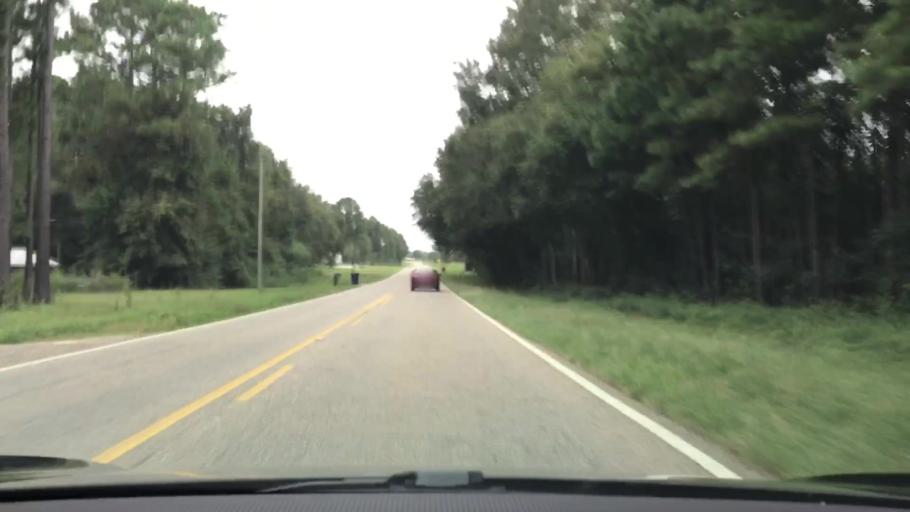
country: US
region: Alabama
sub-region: Geneva County
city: Samson
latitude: 31.1697
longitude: -86.1433
